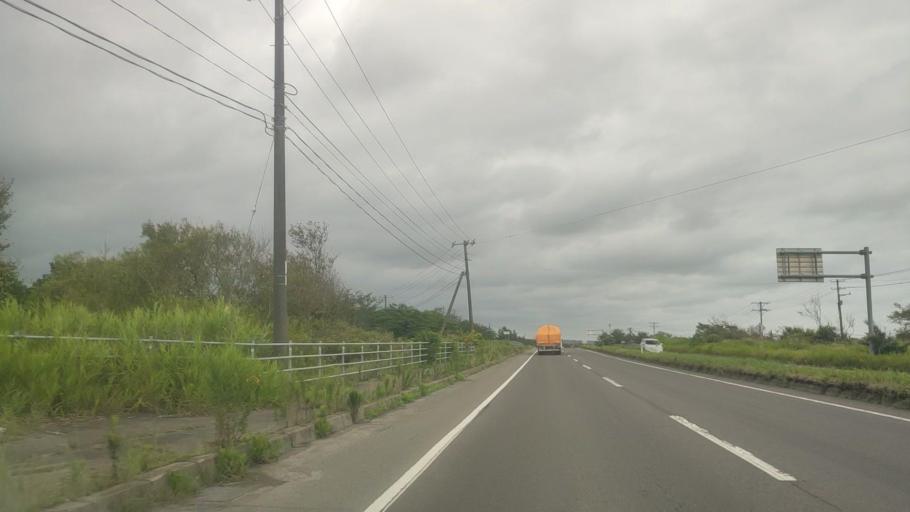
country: JP
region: Hokkaido
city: Shiraoi
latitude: 42.5296
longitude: 141.3224
